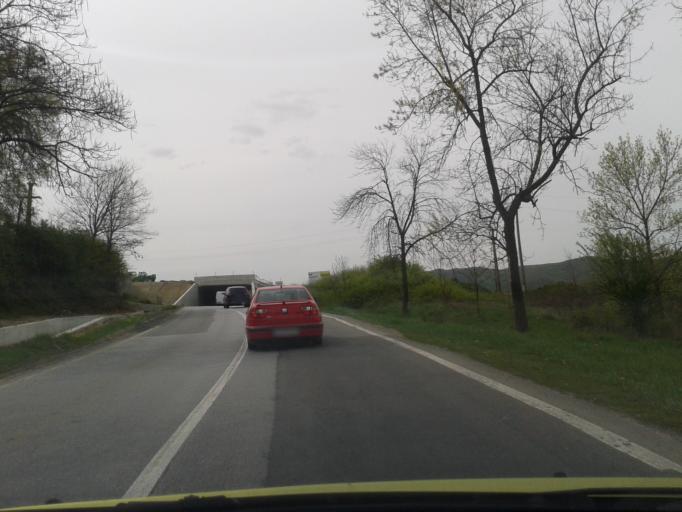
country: RO
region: Hunedoara
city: Lapugiu de Jos
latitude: 45.9124
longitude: 22.5187
